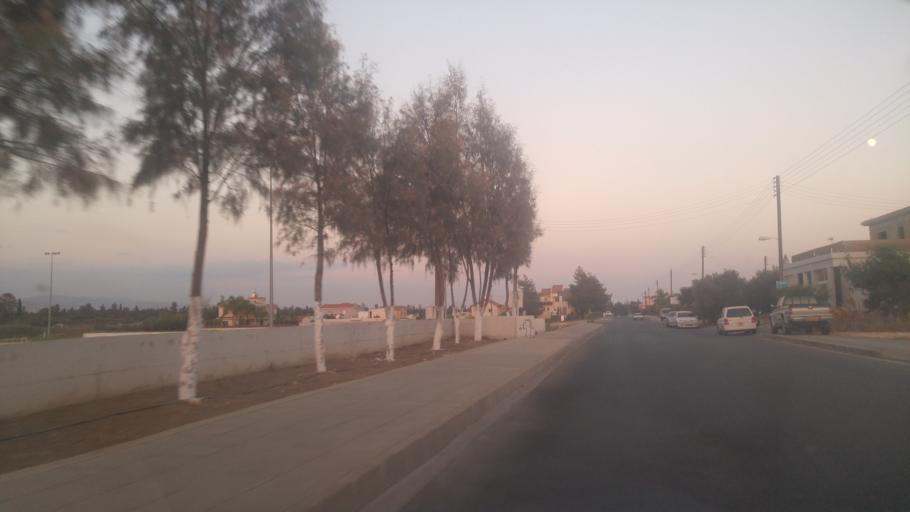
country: CY
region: Limassol
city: Ypsonas
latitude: 34.6608
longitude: 32.9643
